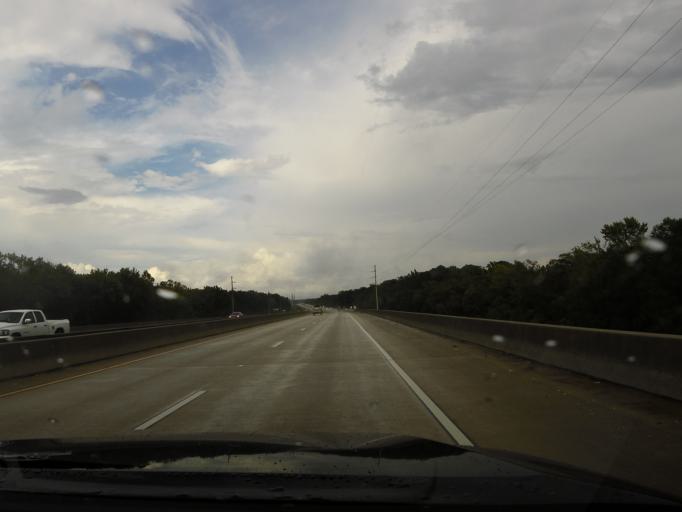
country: US
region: Georgia
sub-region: Wayne County
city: Jesup
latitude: 31.6673
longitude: -81.8370
